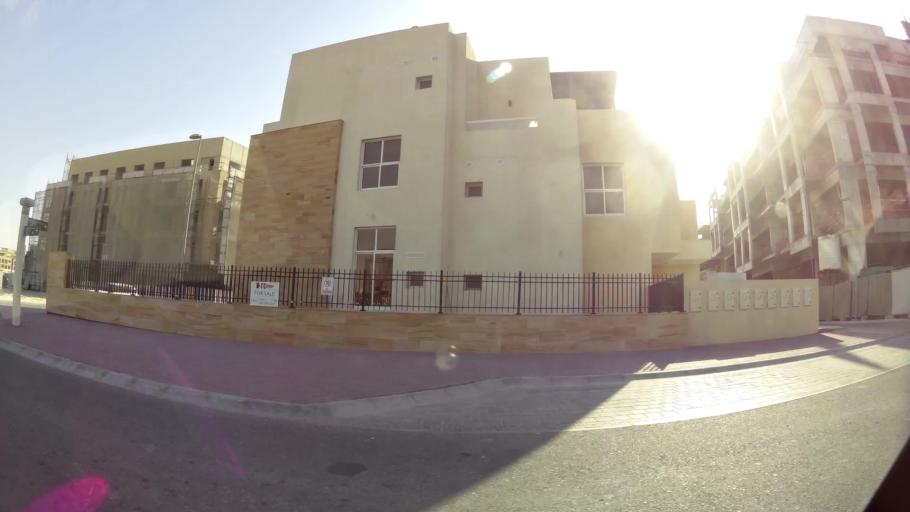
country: AE
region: Dubai
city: Dubai
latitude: 25.0510
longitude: 55.2093
